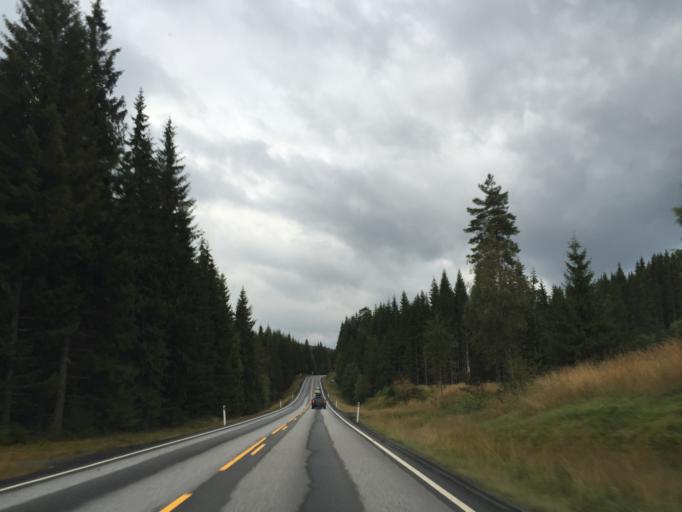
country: NO
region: Hedmark
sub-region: Nord-Odal
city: Sand
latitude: 60.5084
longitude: 11.5092
